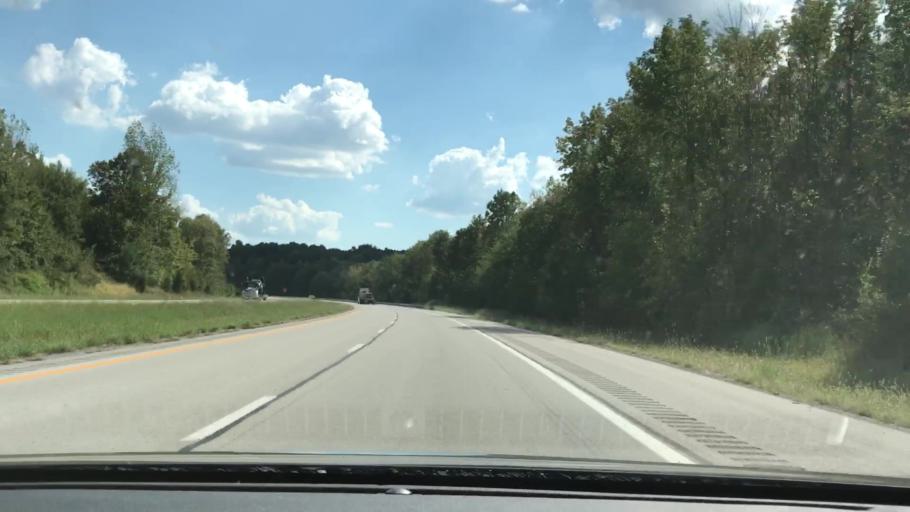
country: US
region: Kentucky
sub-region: Butler County
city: Morgantown
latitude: 37.2651
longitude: -86.7485
